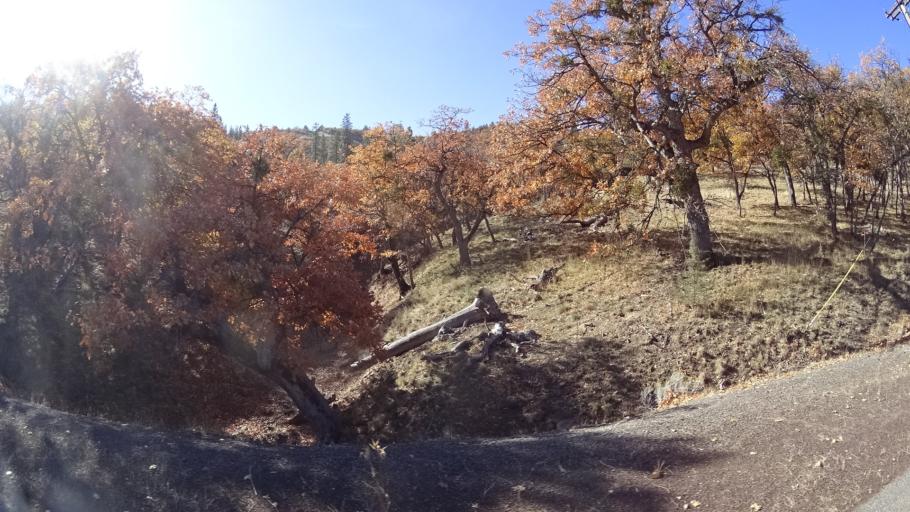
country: US
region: California
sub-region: Siskiyou County
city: Montague
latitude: 41.9792
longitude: -122.3081
